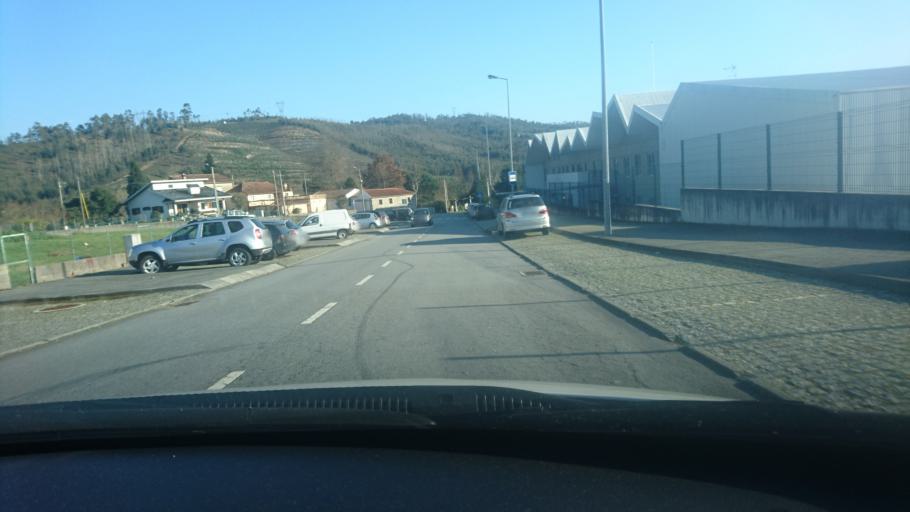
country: PT
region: Porto
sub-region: Paredes
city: Recarei
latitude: 41.1469
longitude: -8.3883
